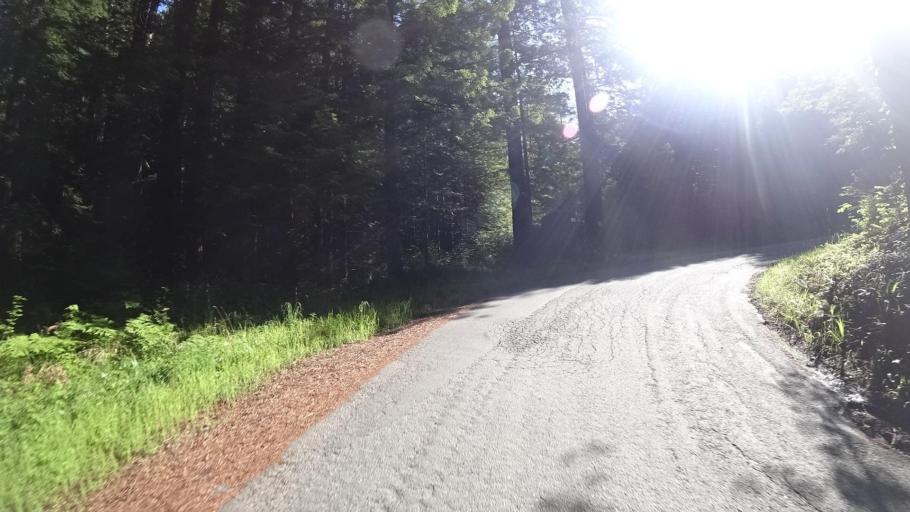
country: US
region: California
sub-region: Humboldt County
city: Rio Dell
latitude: 40.4552
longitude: -124.0266
